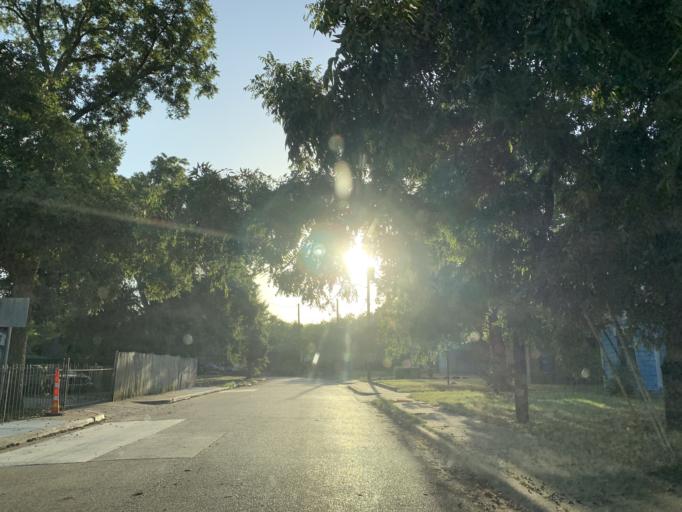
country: US
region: Texas
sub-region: Dallas County
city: Dallas
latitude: 32.7659
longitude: -96.7418
